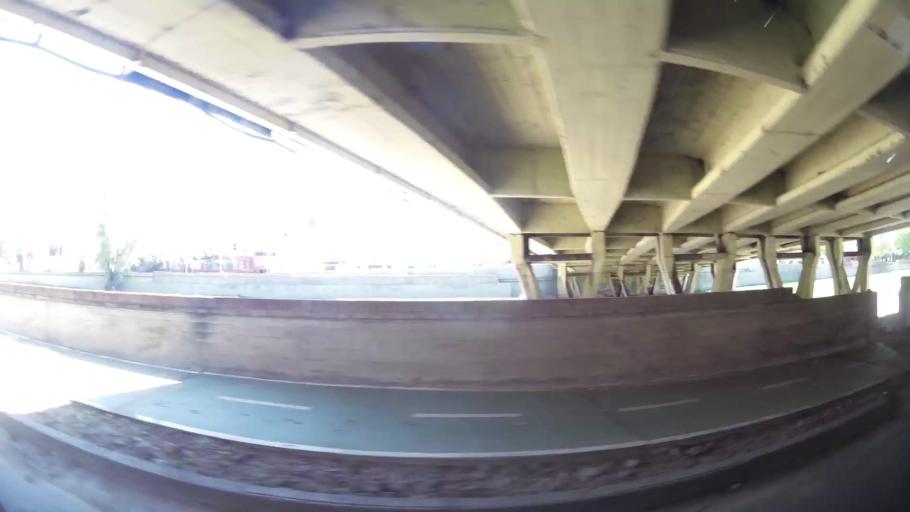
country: AR
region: Cordoba
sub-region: Departamento de Capital
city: Cordoba
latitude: -31.4124
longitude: -64.1745
